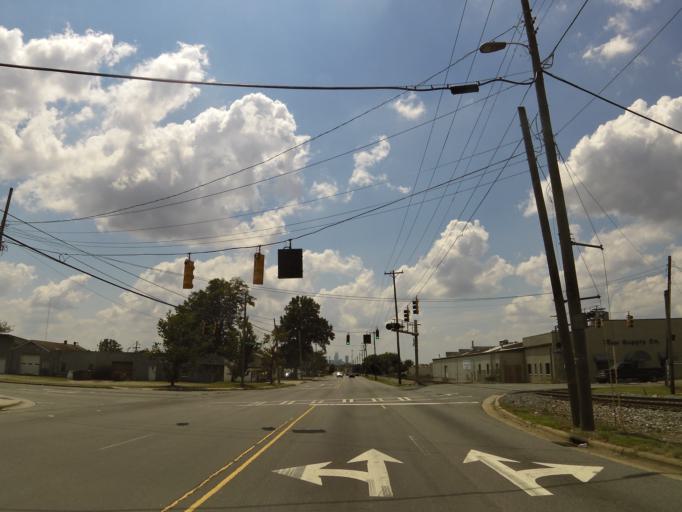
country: US
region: North Carolina
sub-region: Mecklenburg County
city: Charlotte
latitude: 35.2740
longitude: -80.8111
